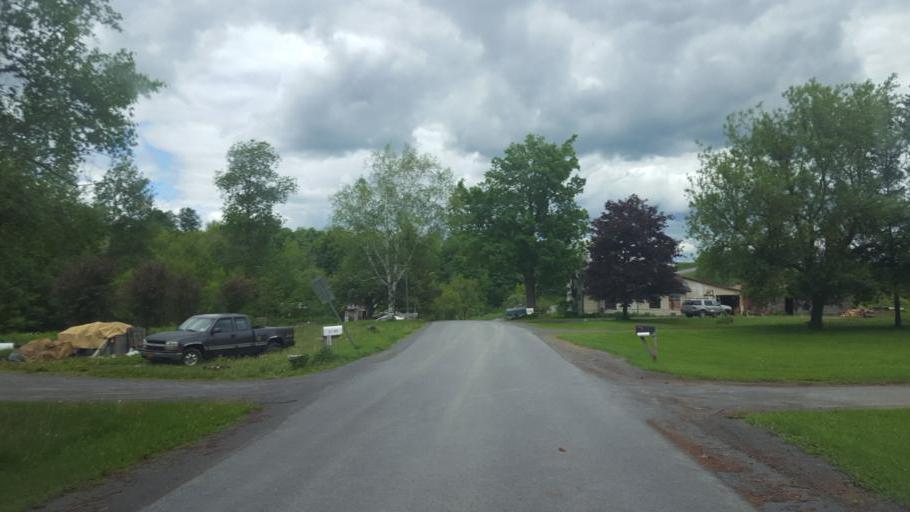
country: US
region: New York
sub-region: Otsego County
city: Richfield Springs
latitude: 42.8680
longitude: -75.0285
